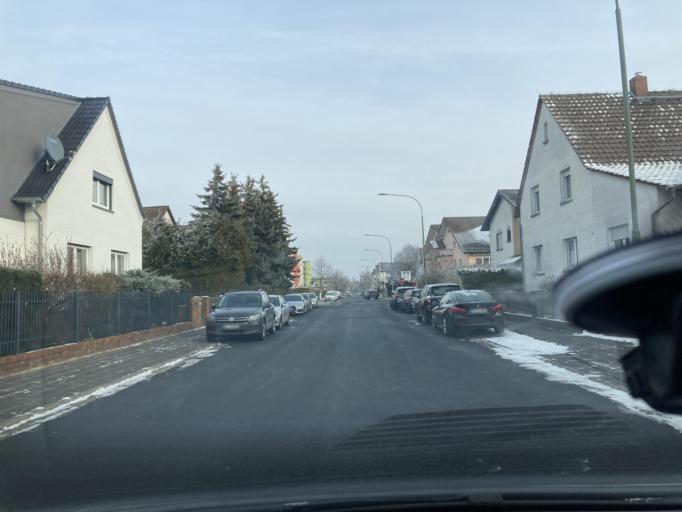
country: DE
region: Hesse
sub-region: Regierungsbezirk Darmstadt
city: Muehlheim am Main
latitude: 50.1083
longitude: 8.8331
